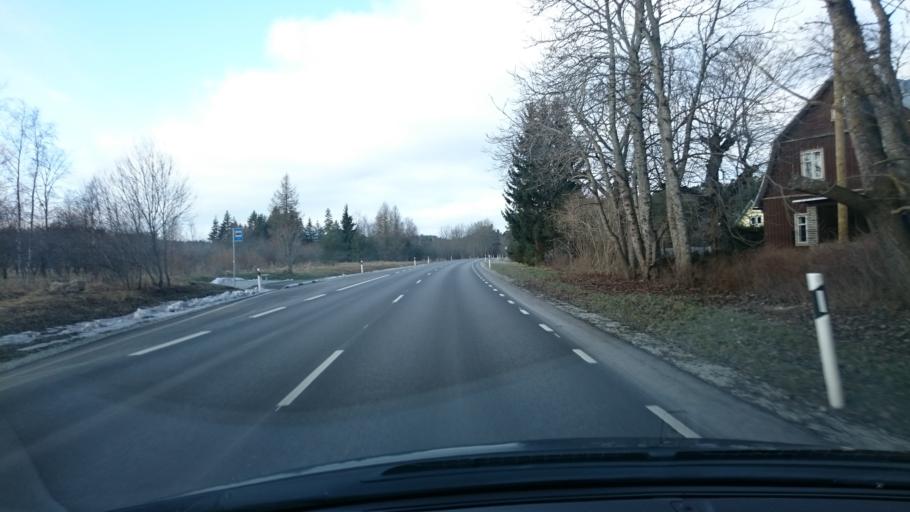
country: EE
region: Harju
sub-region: Keila linn
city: Keila
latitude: 59.3942
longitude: 24.2842
